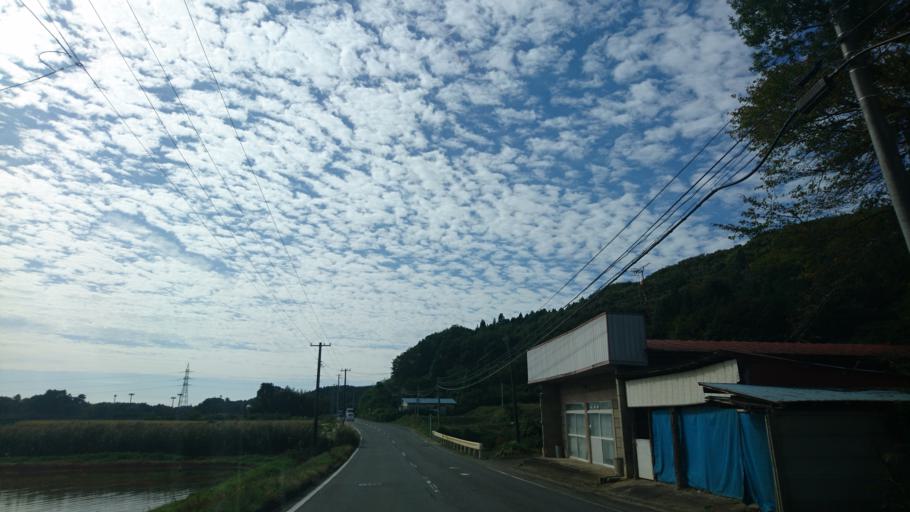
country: JP
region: Fukushima
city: Sukagawa
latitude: 37.3160
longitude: 140.2671
